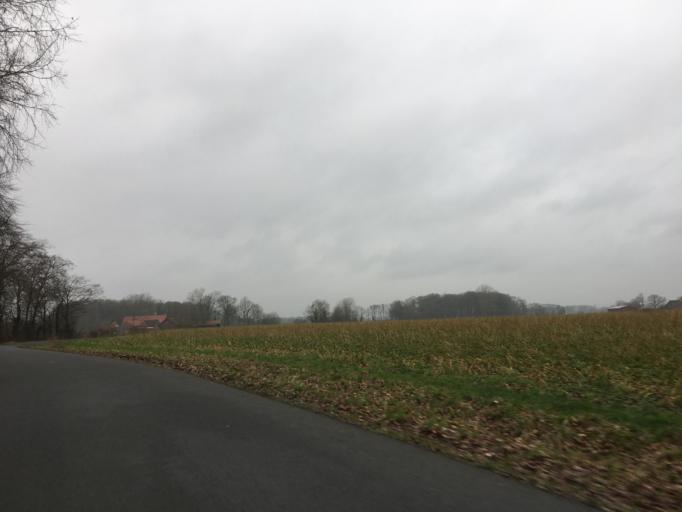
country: DE
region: North Rhine-Westphalia
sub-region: Regierungsbezirk Munster
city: Senden
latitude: 51.8615
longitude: 7.4630
